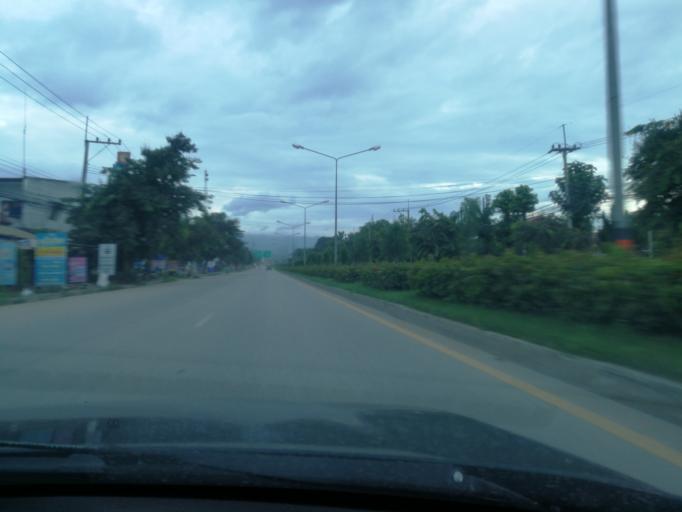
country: TH
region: Chiang Mai
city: Hot
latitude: 18.1887
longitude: 98.6125
